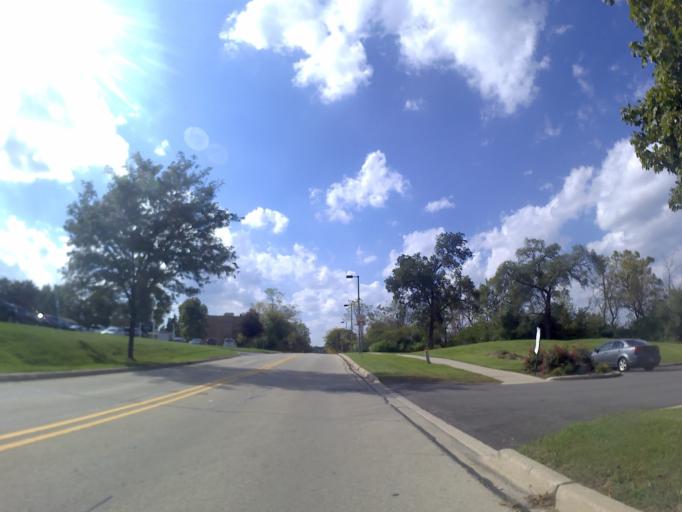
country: US
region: Illinois
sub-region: DuPage County
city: Lisle
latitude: 41.7976
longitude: -88.0699
